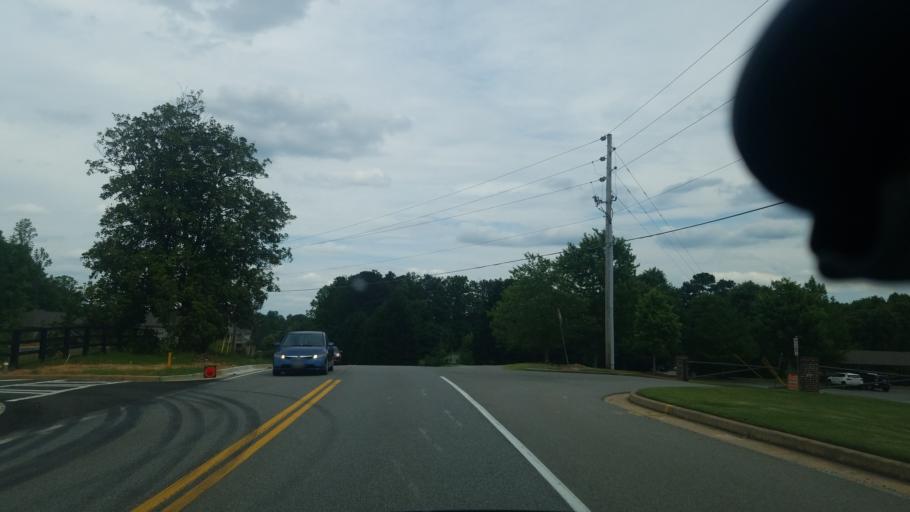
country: US
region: Georgia
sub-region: Forsyth County
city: Cumming
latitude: 34.1524
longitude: -84.1676
